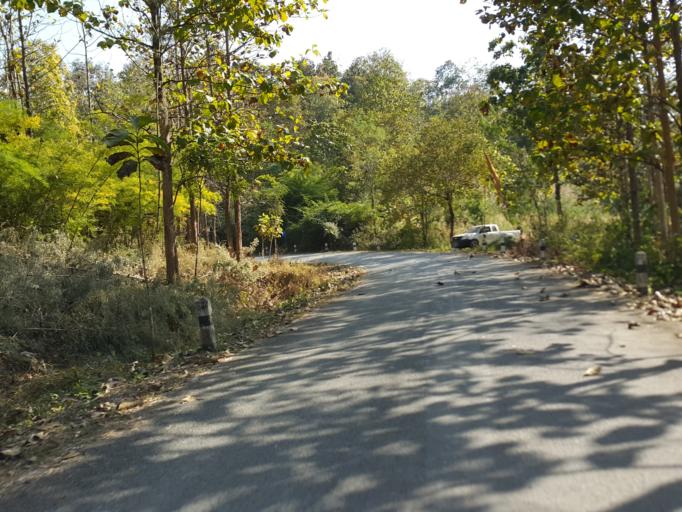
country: TH
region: Chiang Mai
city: Mae On
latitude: 18.7939
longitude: 99.2323
